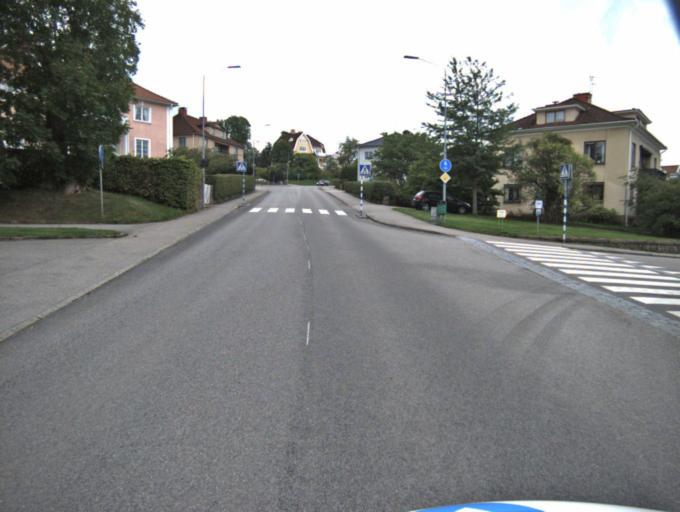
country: SE
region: Vaestra Goetaland
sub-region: Ulricehamns Kommun
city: Ulricehamn
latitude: 57.7902
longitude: 13.4134
